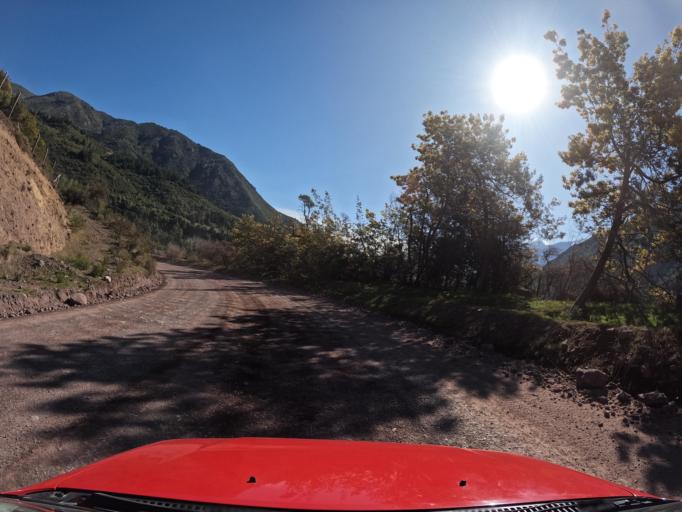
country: CL
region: O'Higgins
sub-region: Provincia de Colchagua
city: Chimbarongo
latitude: -35.0107
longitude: -70.7444
